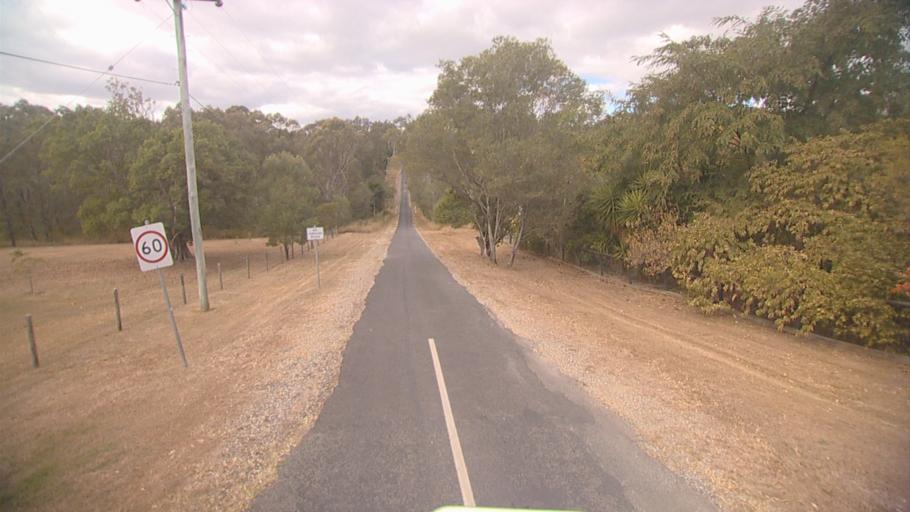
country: AU
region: Queensland
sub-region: Logan
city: Cedar Vale
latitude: -27.8824
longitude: 153.0279
